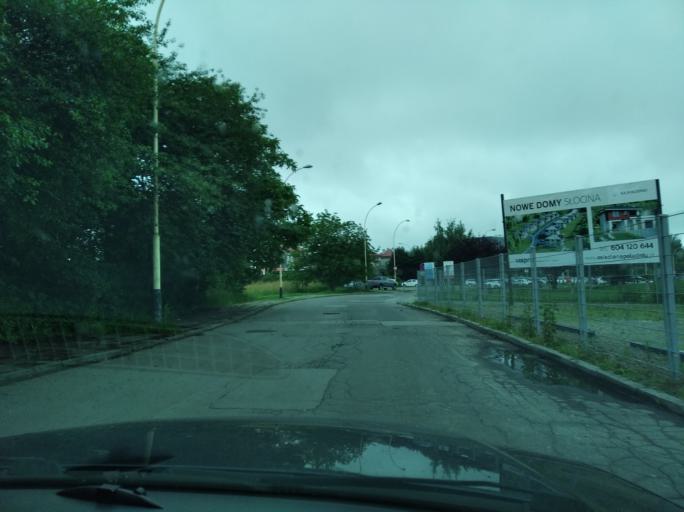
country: PL
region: Subcarpathian Voivodeship
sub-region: Rzeszow
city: Rzeszow
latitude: 50.0339
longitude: 22.0347
